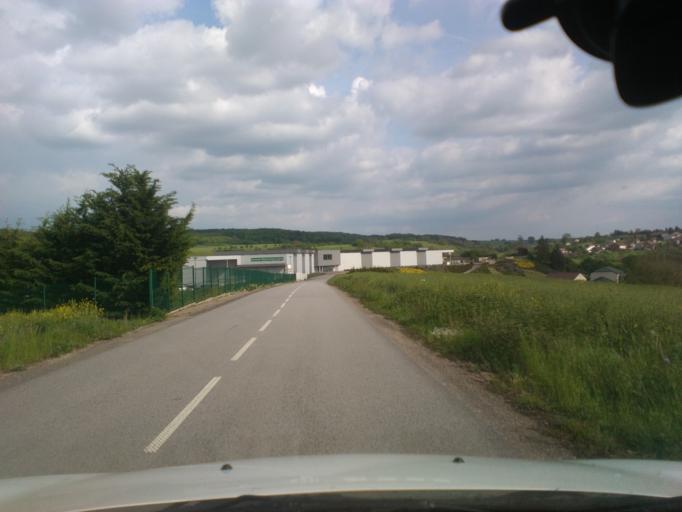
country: FR
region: Lorraine
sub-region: Departement des Vosges
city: Mirecourt
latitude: 48.3316
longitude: 6.1421
